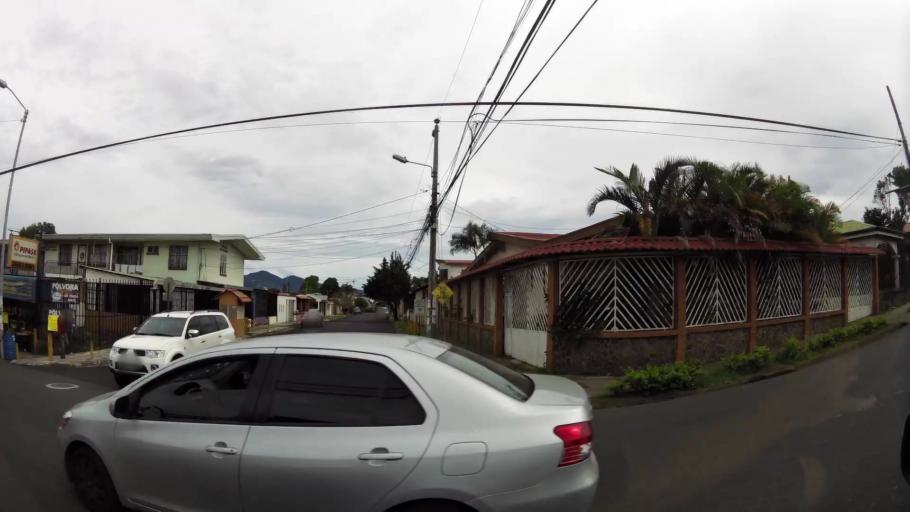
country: CR
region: San Jose
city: Purral
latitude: 9.9495
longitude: -84.0310
